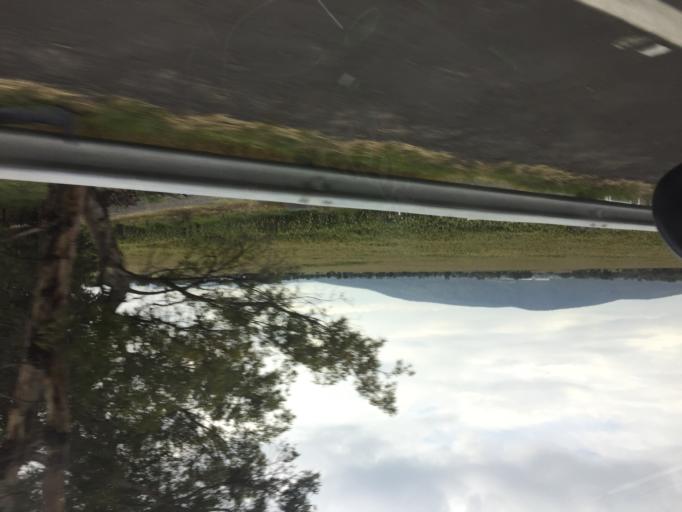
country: MX
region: Jalisco
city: Ocotlan
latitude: 20.3919
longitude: -102.7195
